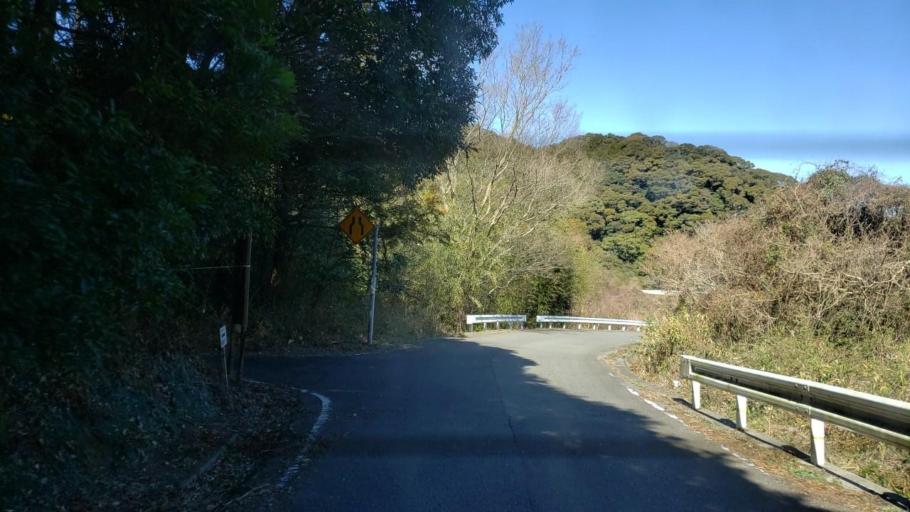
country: JP
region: Tokushima
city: Narutocho-mitsuishi
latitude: 34.2073
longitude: 134.5531
